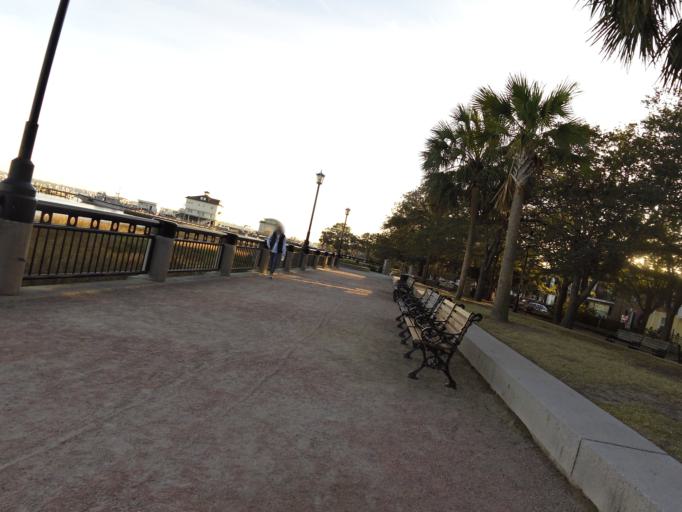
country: US
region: South Carolina
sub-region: Charleston County
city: Charleston
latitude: 32.7772
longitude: -79.9251
